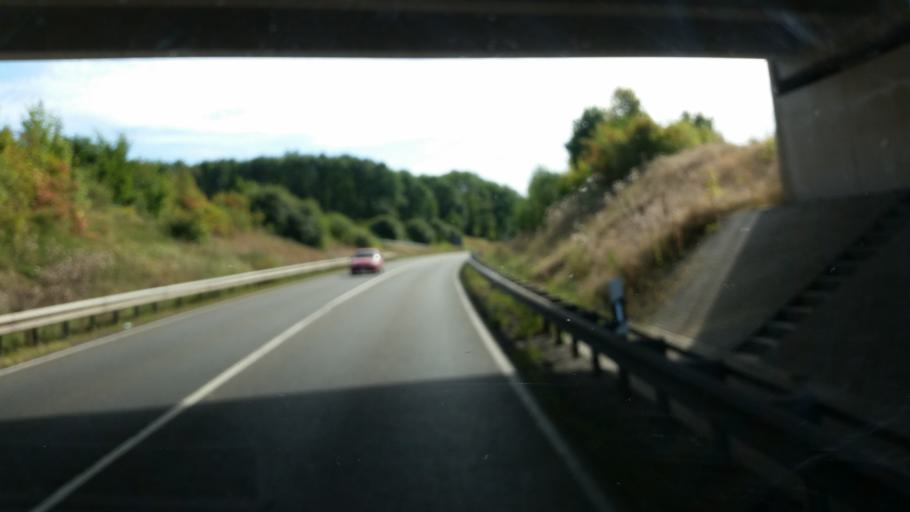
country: DE
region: Rheinland-Pfalz
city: Neuhausel
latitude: 50.3777
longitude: 7.7002
